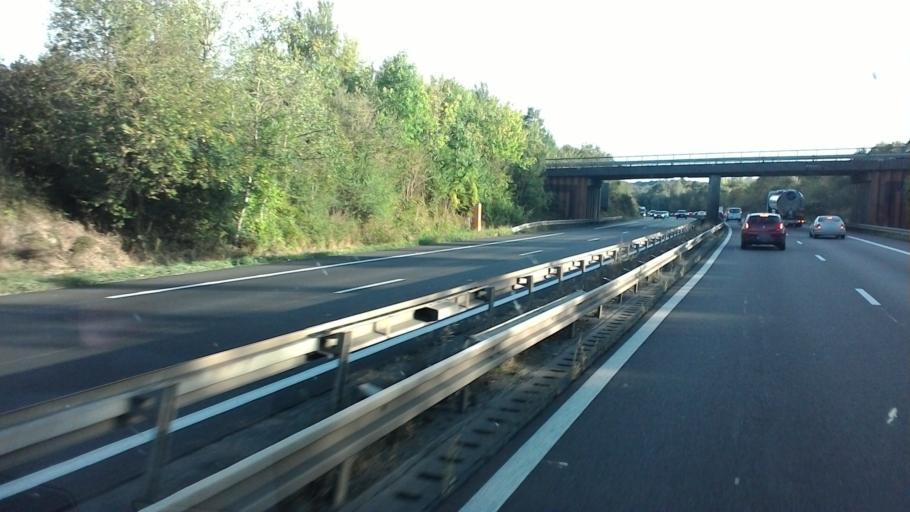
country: FR
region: Lorraine
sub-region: Departement de la Moselle
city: Terville
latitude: 49.3556
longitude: 6.1059
